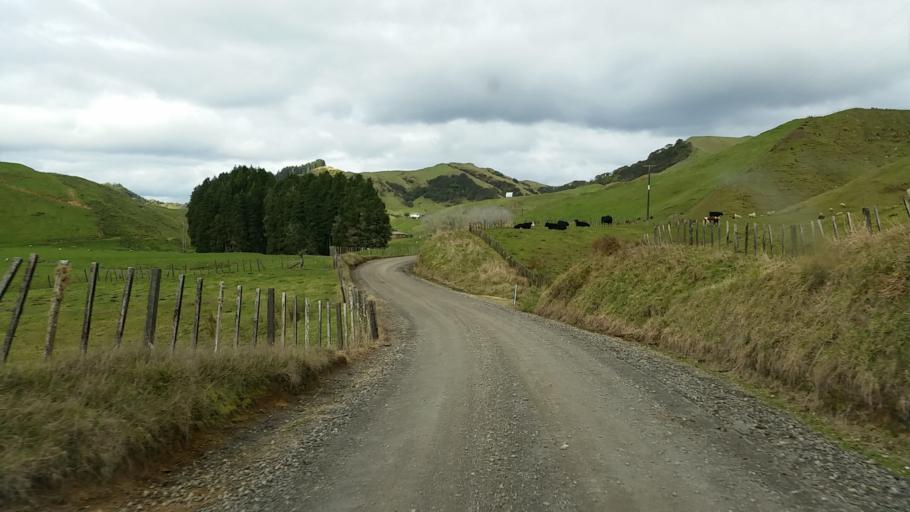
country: NZ
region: Taranaki
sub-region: New Plymouth District
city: Waitara
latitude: -39.1646
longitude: 174.5981
